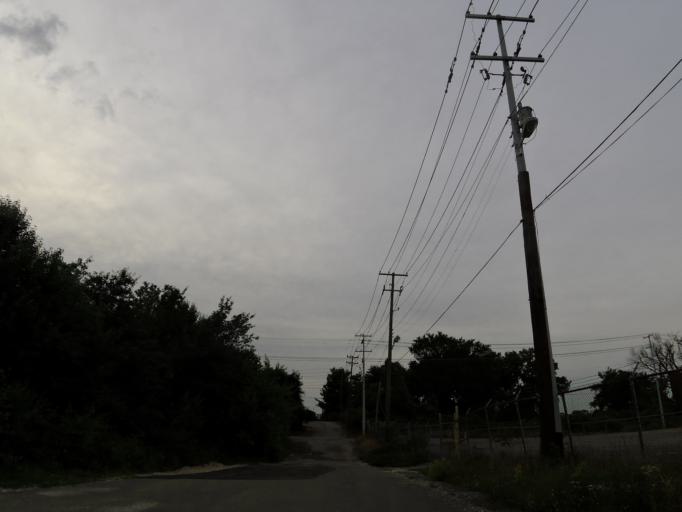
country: US
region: Tennessee
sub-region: Knox County
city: Knoxville
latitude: 35.9608
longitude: -83.9444
